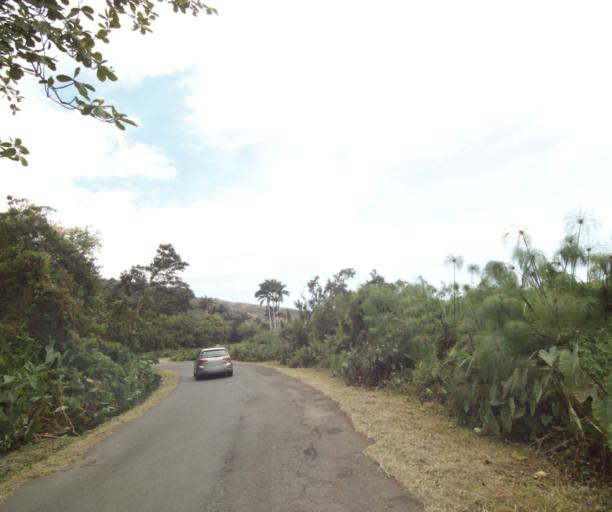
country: RE
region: Reunion
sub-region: Reunion
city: Saint-Paul
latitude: -20.9992
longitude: 55.3022
